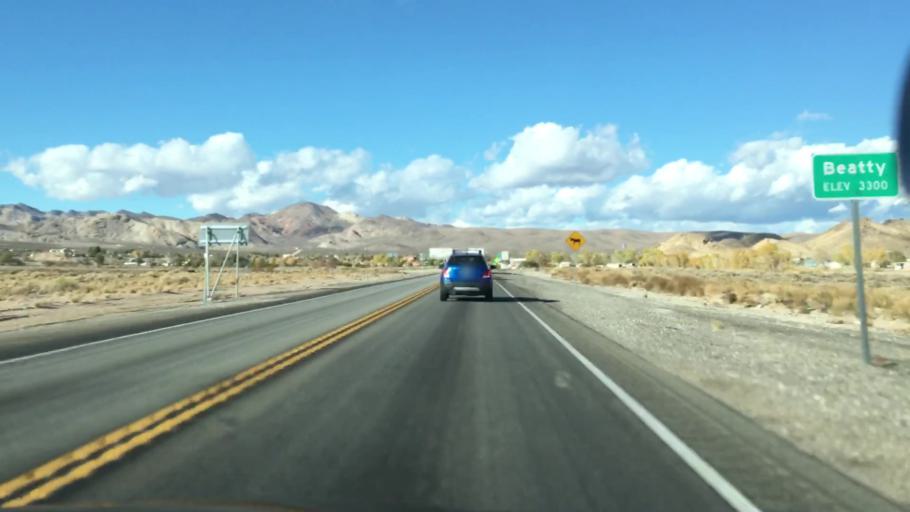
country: US
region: Nevada
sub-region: Nye County
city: Beatty
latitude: 36.8976
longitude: -116.7532
